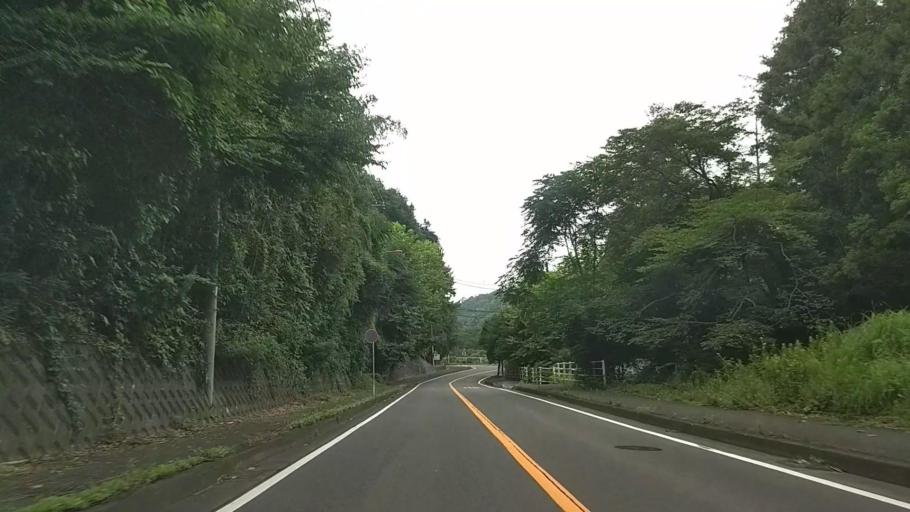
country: JP
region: Kanagawa
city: Hadano
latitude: 35.3393
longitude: 139.2223
